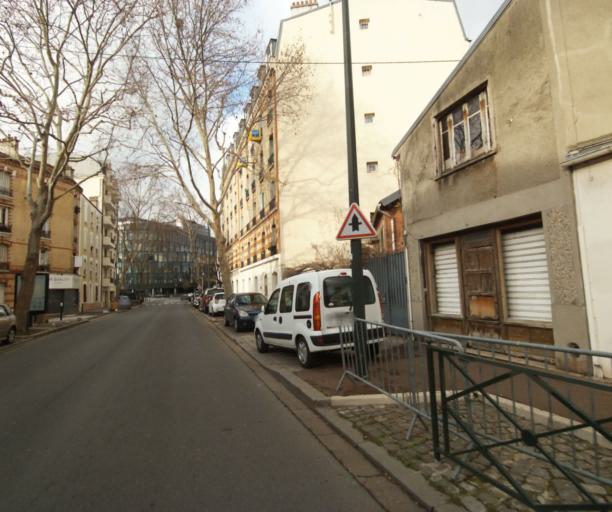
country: FR
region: Ile-de-France
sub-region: Departement des Hauts-de-Seine
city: La Garenne-Colombes
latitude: 48.9041
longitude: 2.2411
